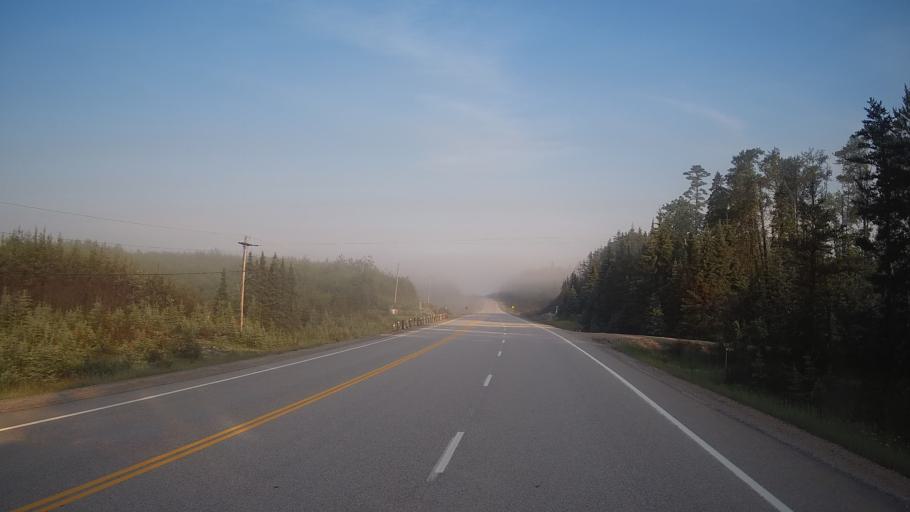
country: CA
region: Ontario
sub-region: Rainy River District
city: Atikokan
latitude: 49.2625
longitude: -91.2209
